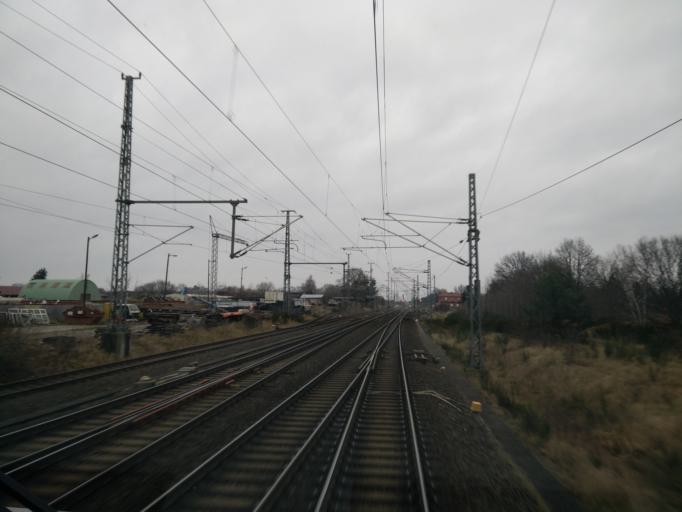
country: DE
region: Mecklenburg-Vorpommern
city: Sulstorf
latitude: 53.5529
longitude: 11.3638
